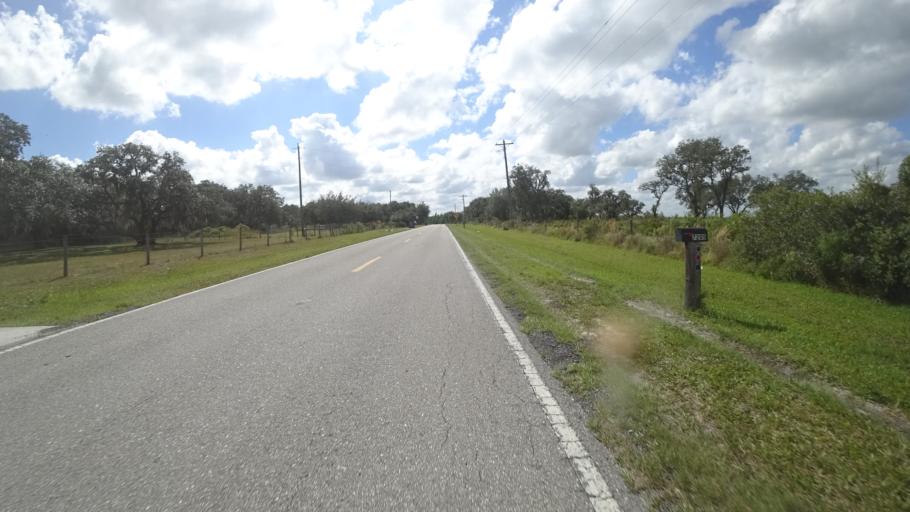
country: US
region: Florida
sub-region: Sarasota County
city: Lake Sarasota
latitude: 27.4107
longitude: -82.1334
